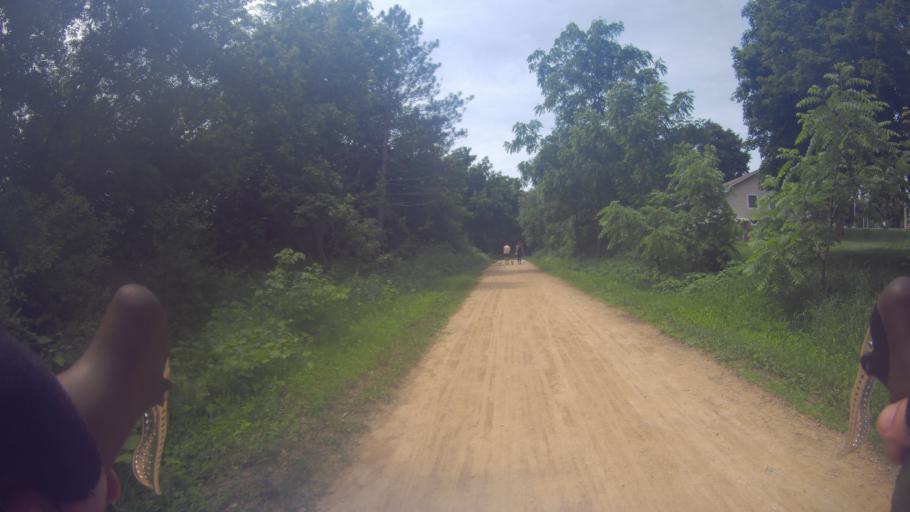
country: US
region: Wisconsin
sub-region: Dane County
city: Mount Horeb
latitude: 43.0088
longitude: -89.7280
